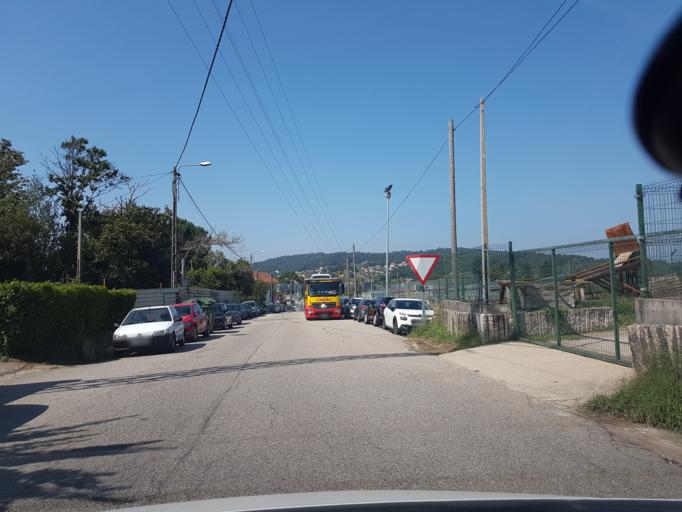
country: ES
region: Galicia
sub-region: Provincia de Pontevedra
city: Porrino
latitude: 42.2217
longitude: -8.6343
